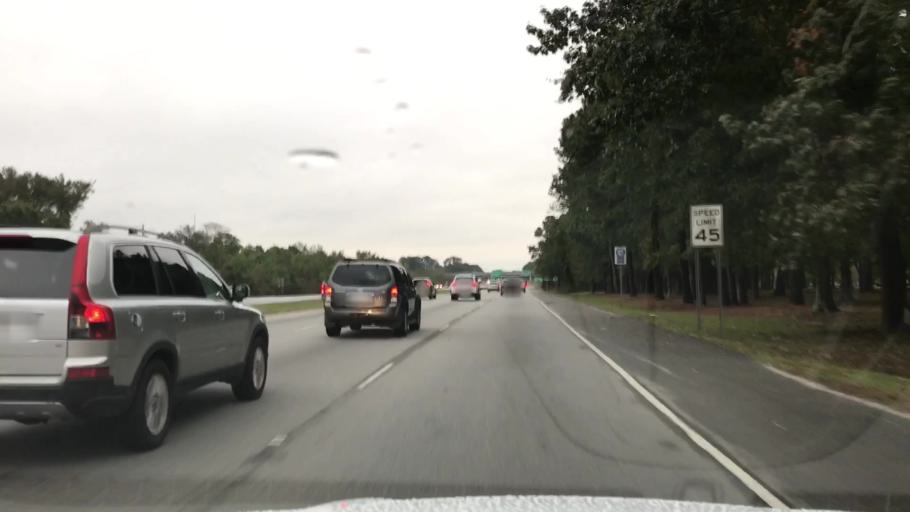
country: US
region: South Carolina
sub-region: Charleston County
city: Shell Point
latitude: 32.8117
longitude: -80.0429
